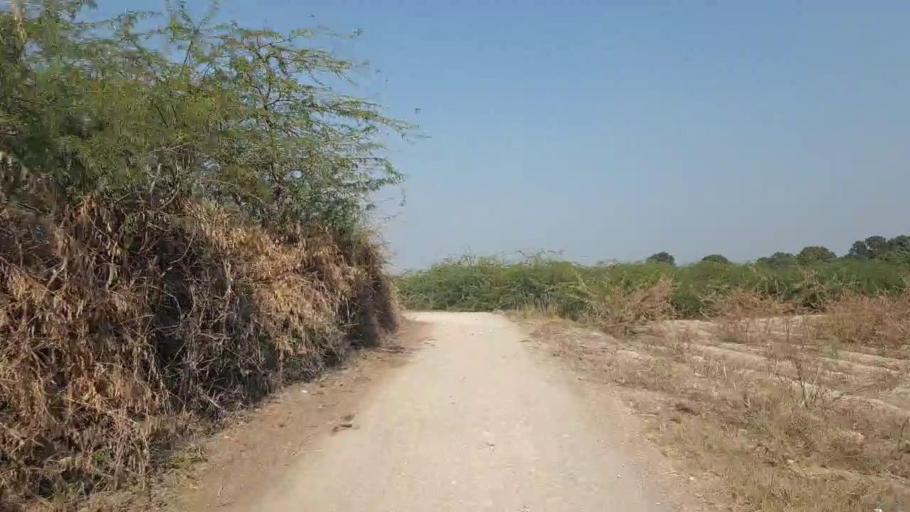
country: PK
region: Sindh
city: Chambar
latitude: 25.4115
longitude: 68.9073
